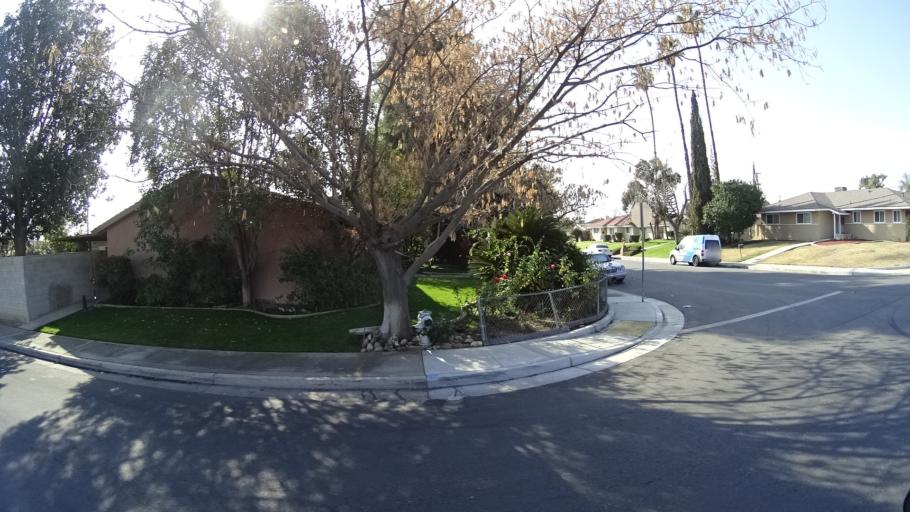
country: US
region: California
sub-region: Kern County
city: Oildale
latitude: 35.4011
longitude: -118.9514
